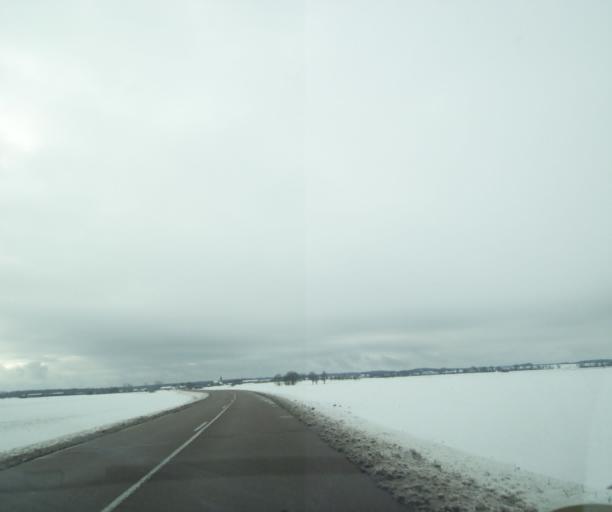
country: FR
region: Champagne-Ardenne
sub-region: Departement de la Haute-Marne
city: Montier-en-Der
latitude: 48.4432
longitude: 4.7328
